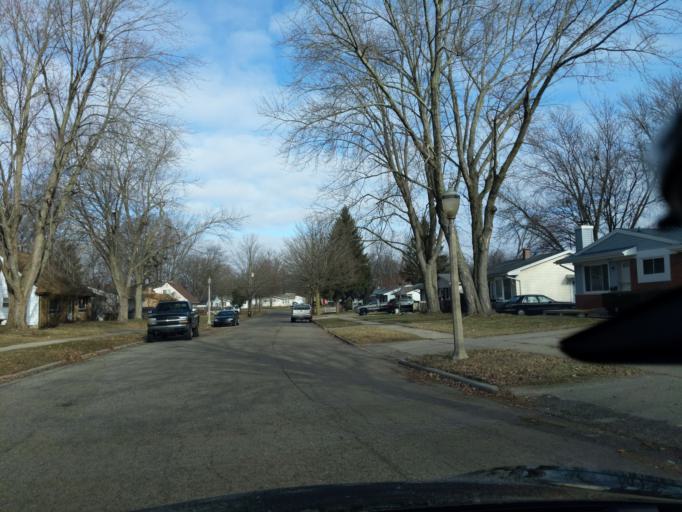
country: US
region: Michigan
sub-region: Eaton County
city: Waverly
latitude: 42.6951
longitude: -84.5998
